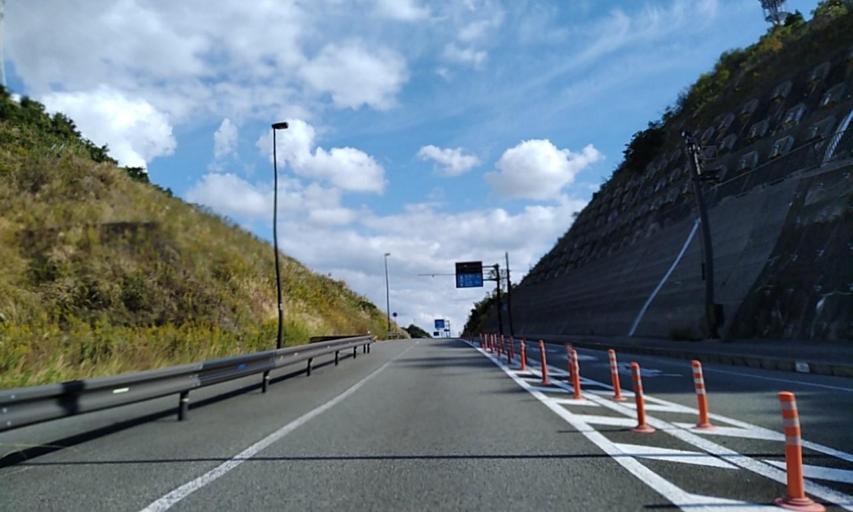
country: JP
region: Wakayama
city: Tanabe
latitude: 33.7502
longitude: 135.3582
